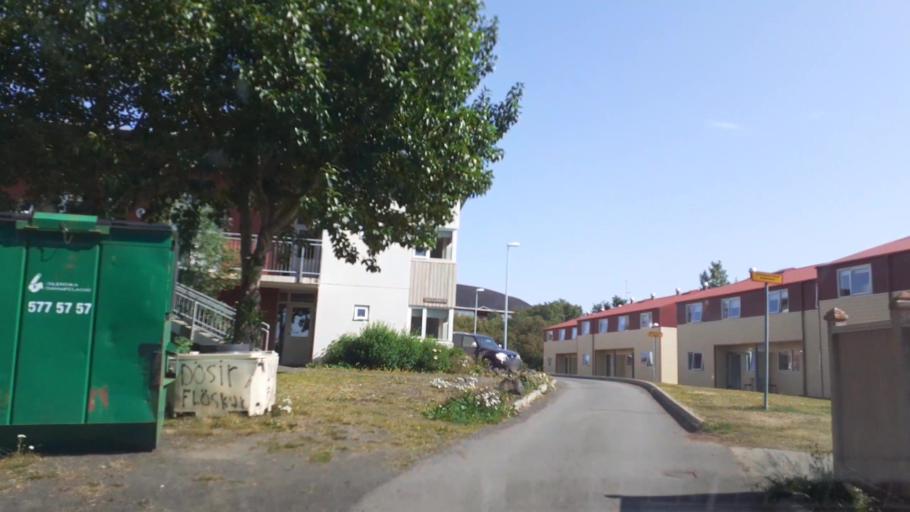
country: IS
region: West
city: Borgarnes
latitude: 64.7673
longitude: -21.5521
